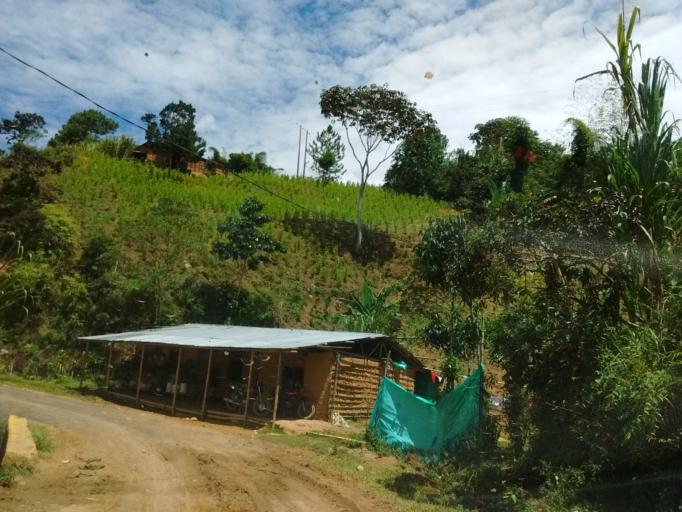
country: CO
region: Cauca
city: Villa Rica
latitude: 2.6549
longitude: -76.7674
